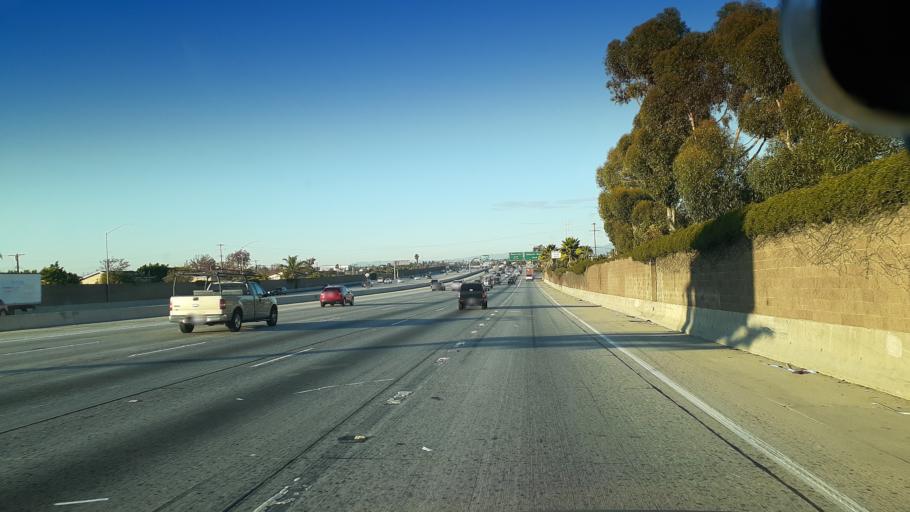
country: US
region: California
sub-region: Los Angeles County
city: West Rancho Dominguez
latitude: 33.8873
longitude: -118.2852
